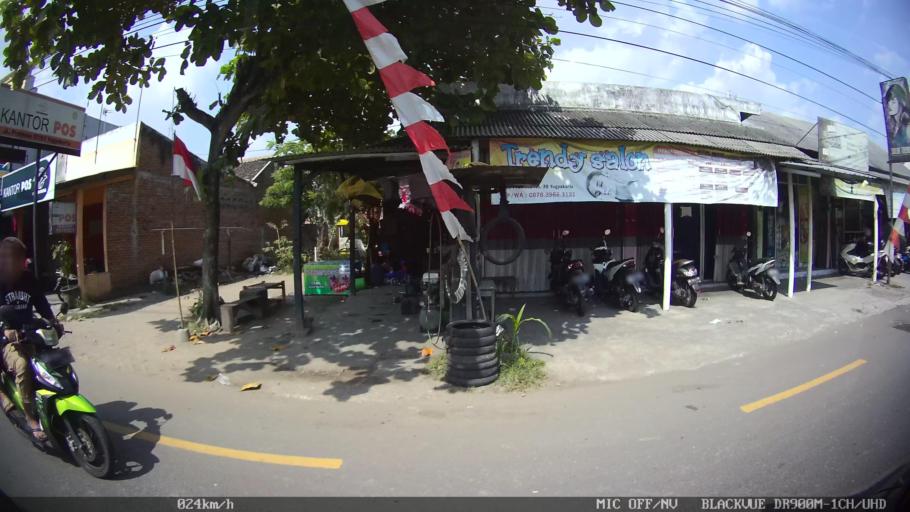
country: ID
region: Daerah Istimewa Yogyakarta
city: Yogyakarta
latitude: -7.8239
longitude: 110.3904
